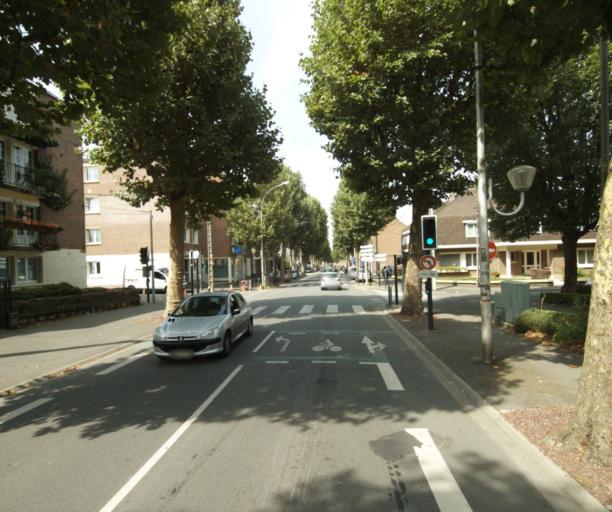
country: FR
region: Nord-Pas-de-Calais
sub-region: Departement du Nord
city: Loos
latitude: 50.6088
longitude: 3.0151
